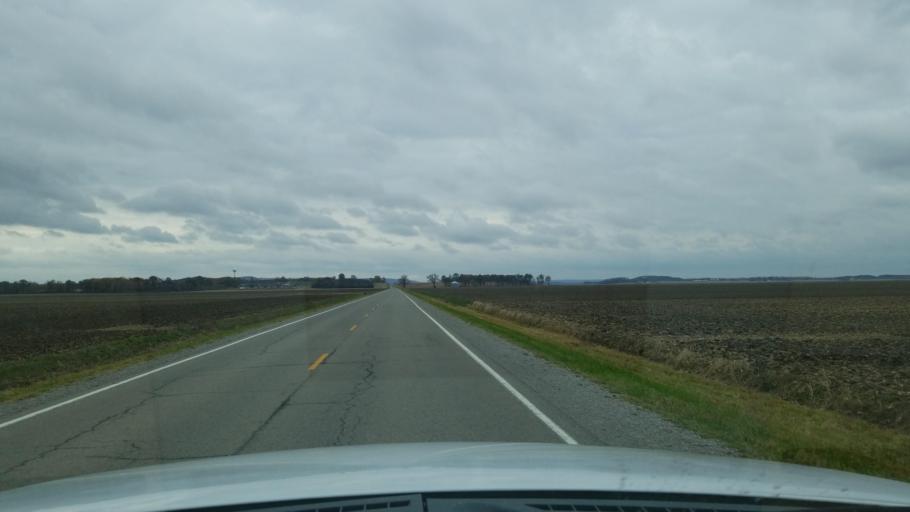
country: US
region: Illinois
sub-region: Saline County
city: Eldorado
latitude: 37.7695
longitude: -88.4382
